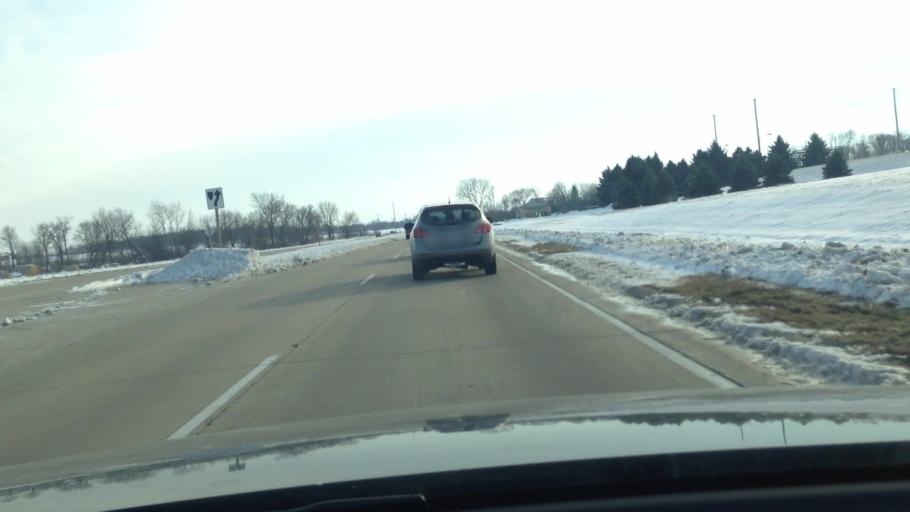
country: US
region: Wisconsin
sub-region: Walworth County
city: Lake Geneva
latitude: 42.5805
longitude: -88.4119
